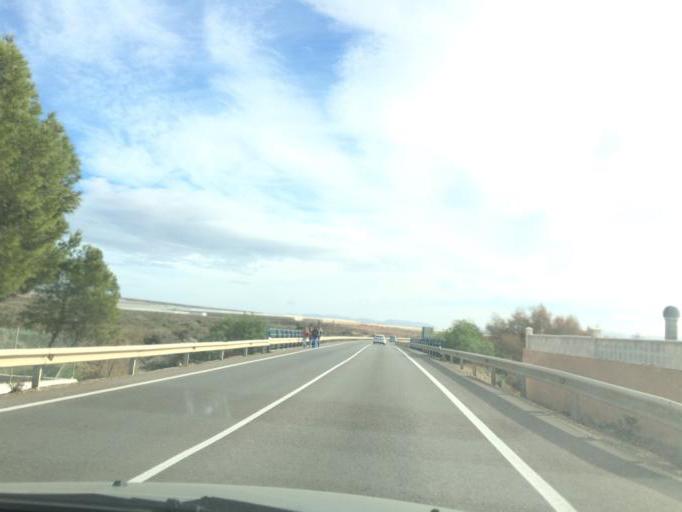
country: ES
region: Andalusia
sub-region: Provincia de Almeria
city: Retamar
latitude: 36.8434
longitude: -2.3010
